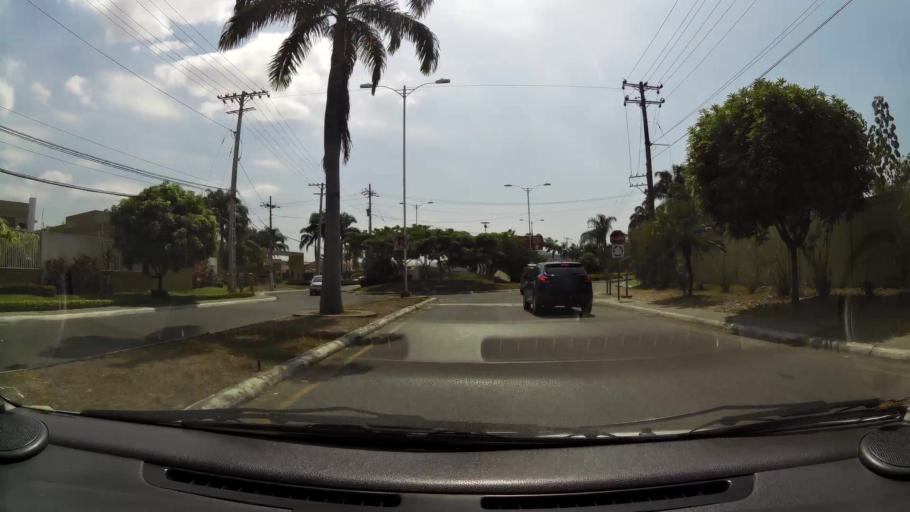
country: EC
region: Guayas
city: El Triunfo
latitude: -2.0410
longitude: -79.8933
